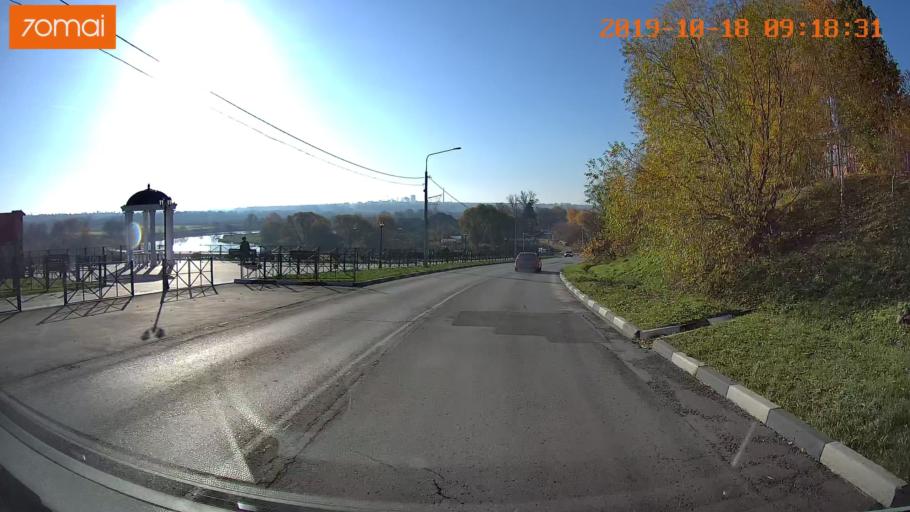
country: RU
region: Tula
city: Yefremov
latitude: 53.1366
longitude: 38.1206
